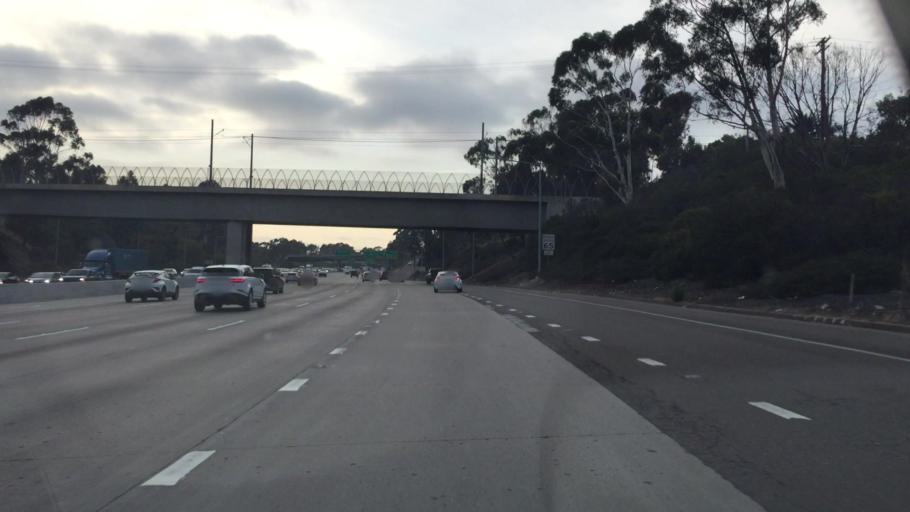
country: US
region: California
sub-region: San Diego County
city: National City
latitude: 32.7069
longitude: -117.0963
